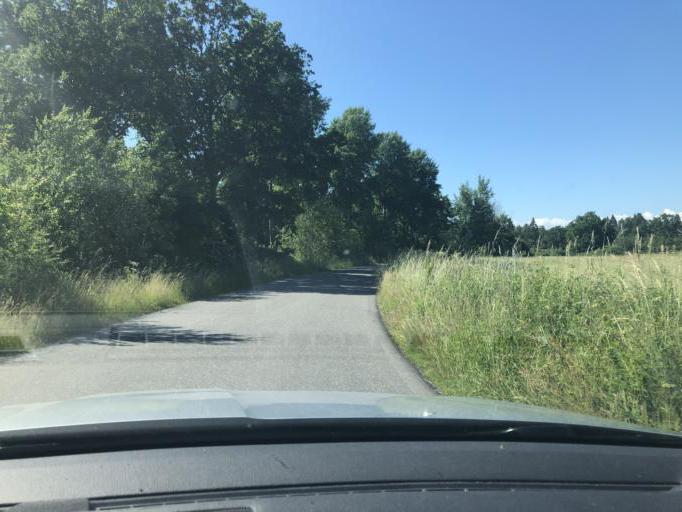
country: SE
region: Blekinge
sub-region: Karlshamns Kommun
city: Karlshamn
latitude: 56.1686
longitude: 14.8132
